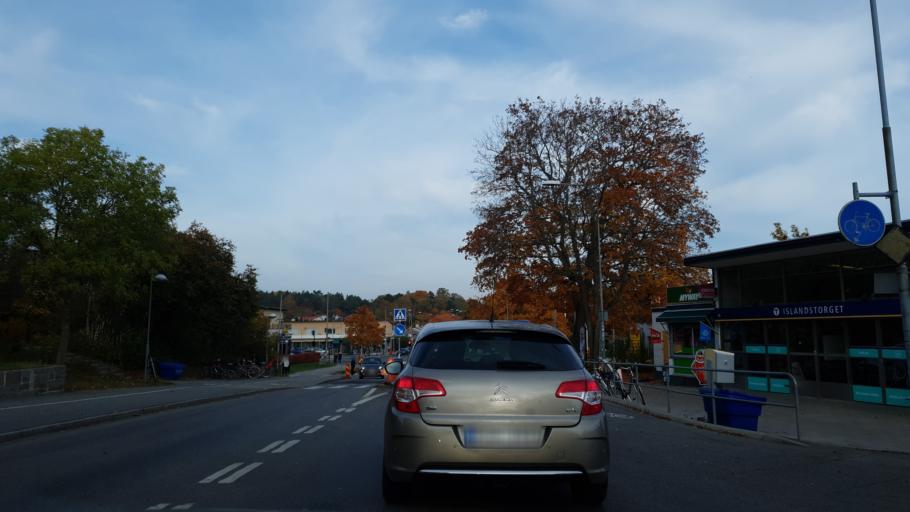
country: SE
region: Stockholm
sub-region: Stockholms Kommun
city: Bromma
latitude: 59.3459
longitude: 17.8927
